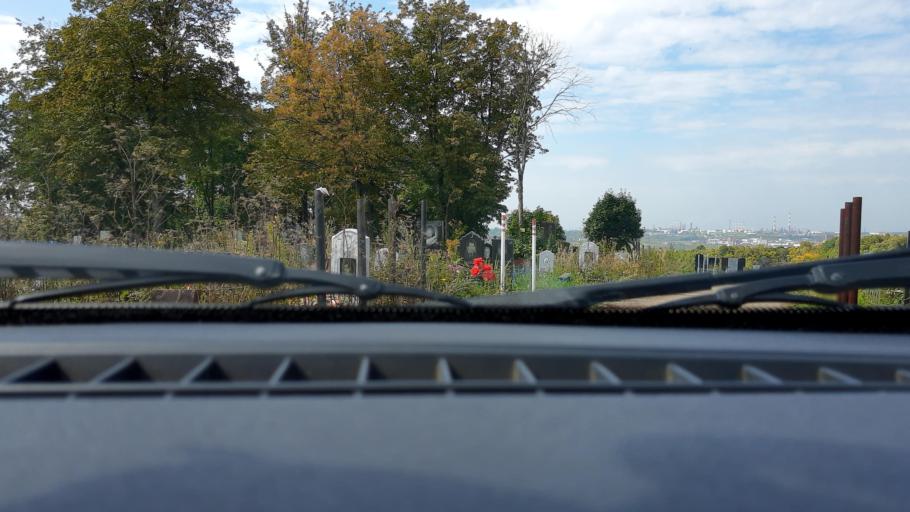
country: RU
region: Bashkortostan
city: Ufa
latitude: 54.8614
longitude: 56.1658
